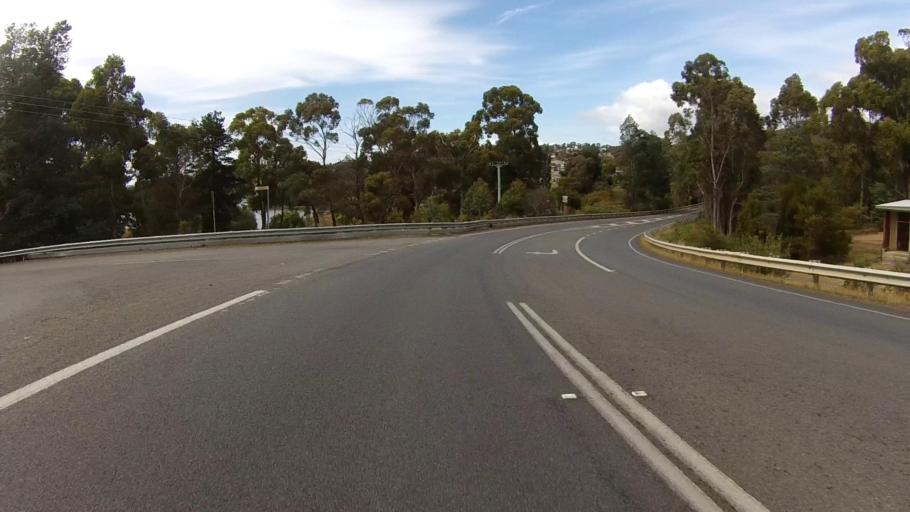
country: AU
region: Tasmania
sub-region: Kingborough
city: Kettering
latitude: -43.1207
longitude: 147.2461
